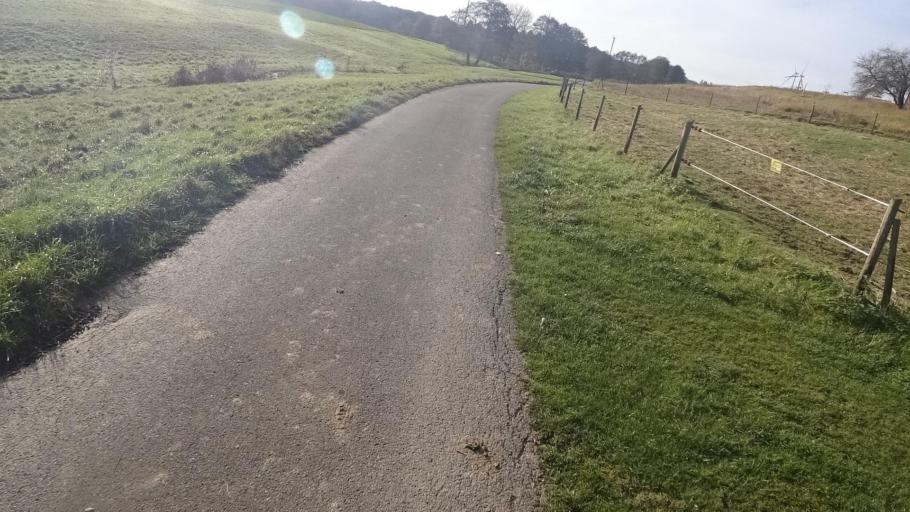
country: DE
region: Rheinland-Pfalz
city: Hausbay
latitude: 50.1057
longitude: 7.5554
